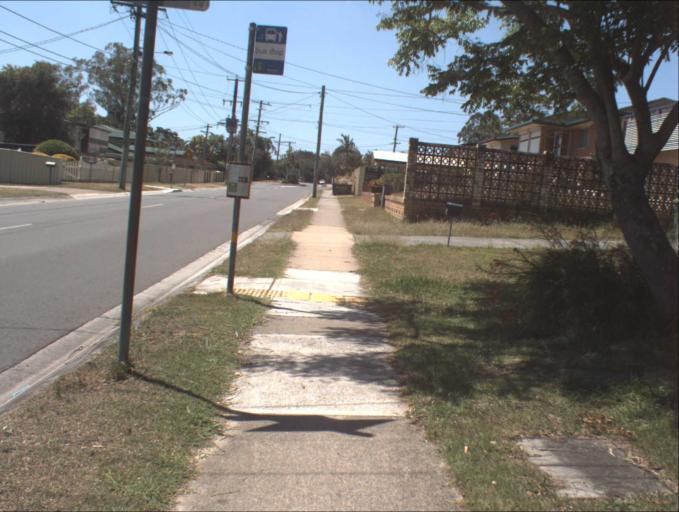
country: AU
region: Queensland
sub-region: Logan
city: Rochedale South
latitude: -27.5990
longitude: 153.1272
